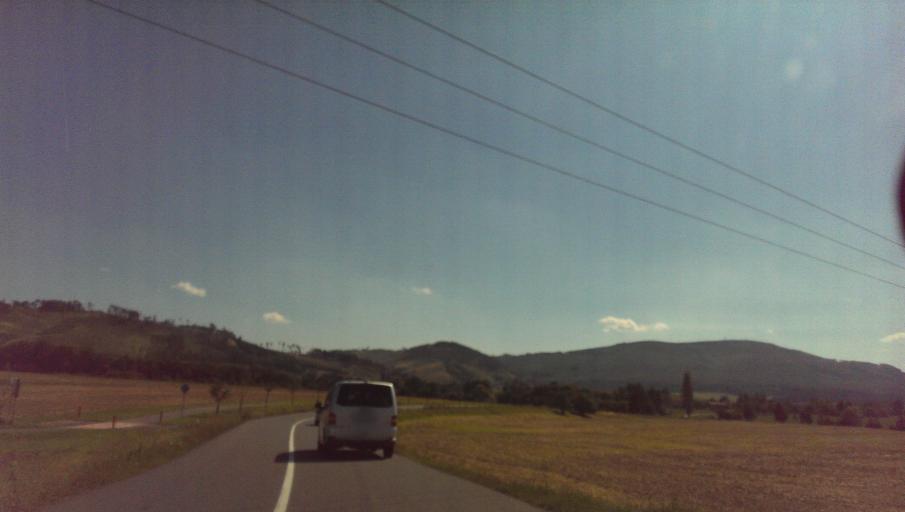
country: CZ
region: Zlin
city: Kelc
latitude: 49.4372
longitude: 17.8034
